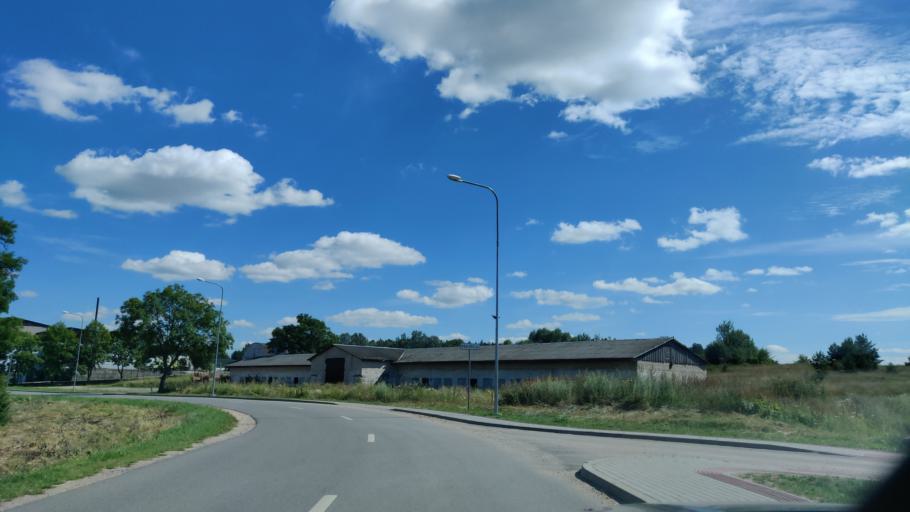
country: LT
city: Salcininkai
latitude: 54.4329
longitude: 25.3025
